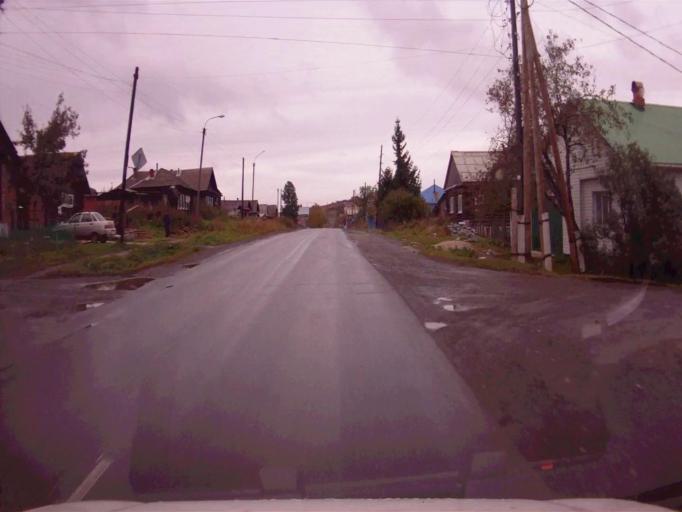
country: RU
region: Chelyabinsk
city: Verkhniy Ufaley
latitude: 56.0555
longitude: 60.2043
